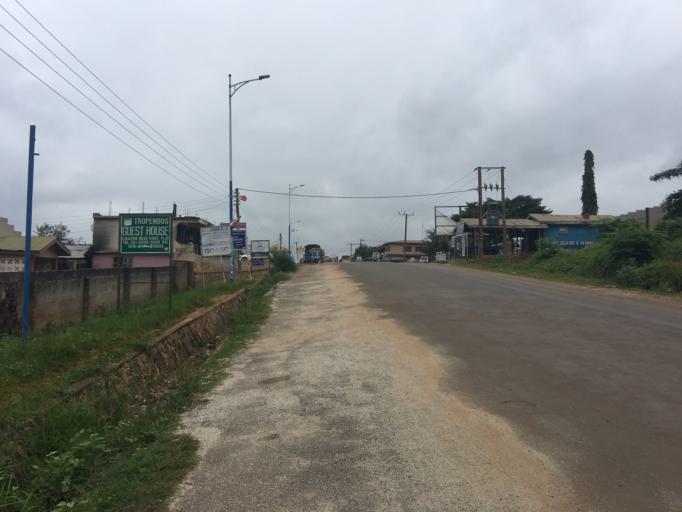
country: GH
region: Western
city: Bibiani
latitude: 6.8058
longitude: -2.5123
